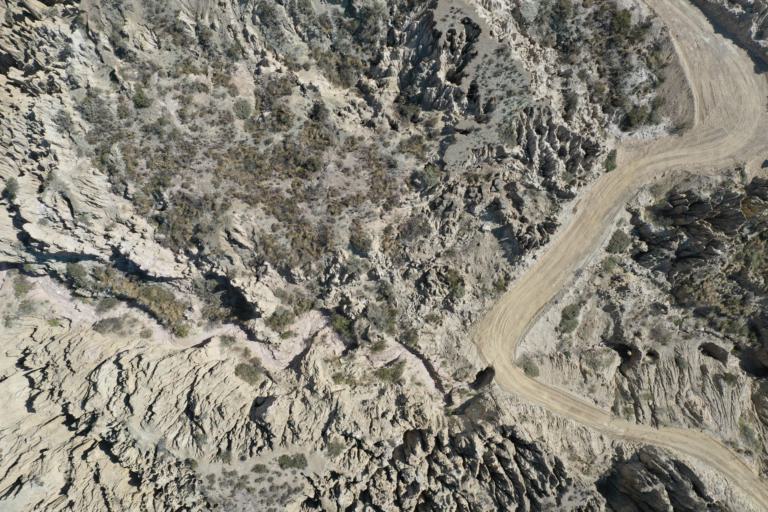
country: BO
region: La Paz
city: La Paz
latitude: -16.5628
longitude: -68.1287
